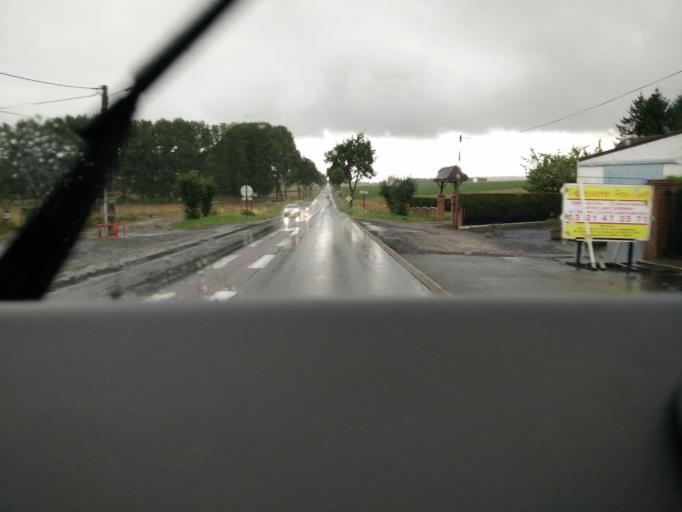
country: FR
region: Nord-Pas-de-Calais
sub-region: Departement du Pas-de-Calais
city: Savy-Berlette
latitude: 50.3534
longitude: 2.4936
